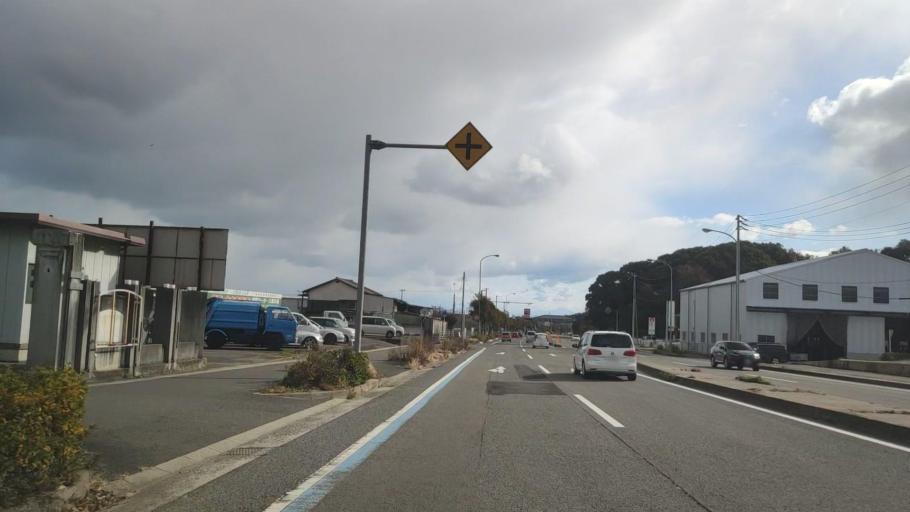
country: JP
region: Ehime
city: Hojo
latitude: 34.0620
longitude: 132.9603
